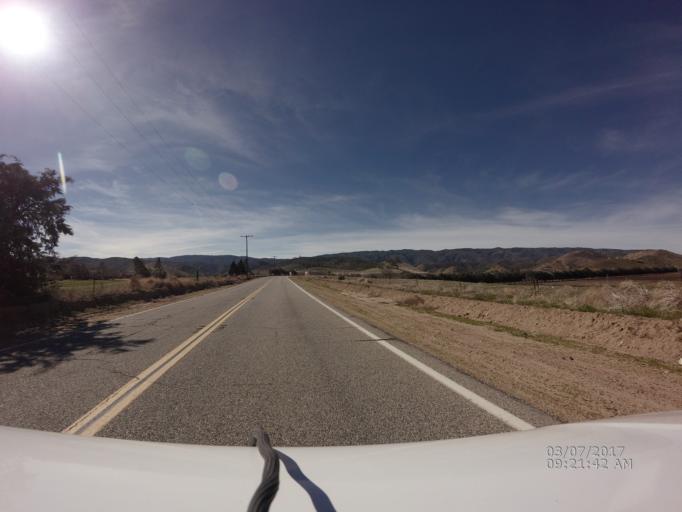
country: US
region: California
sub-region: Los Angeles County
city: Green Valley
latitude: 34.7691
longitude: -118.5900
